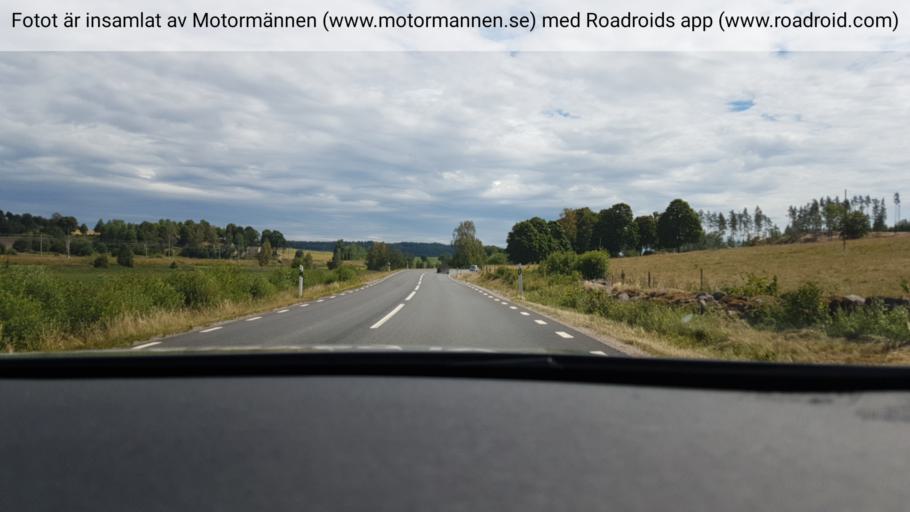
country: SE
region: Joenkoeping
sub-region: Tranas Kommun
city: Tranas
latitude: 57.9964
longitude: 14.8990
